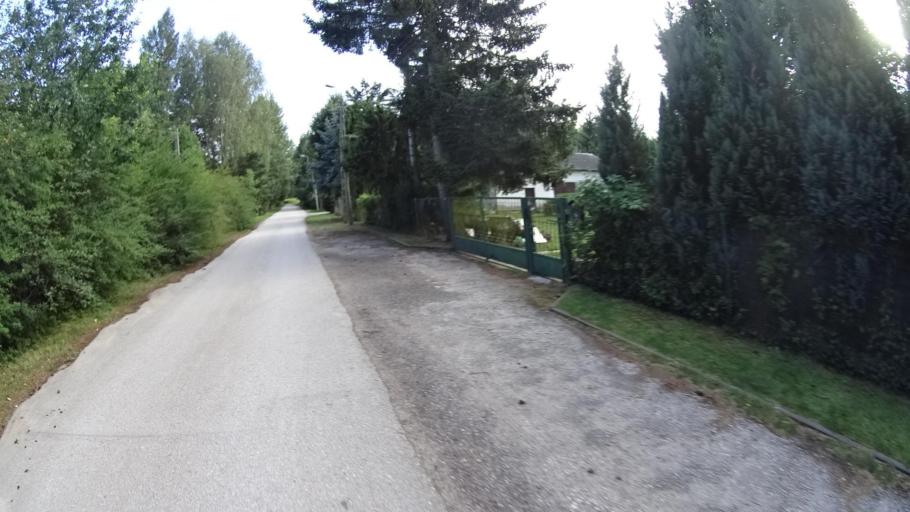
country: PL
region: Masovian Voivodeship
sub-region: Powiat piaseczynski
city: Tarczyn
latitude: 51.9740
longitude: 20.8693
